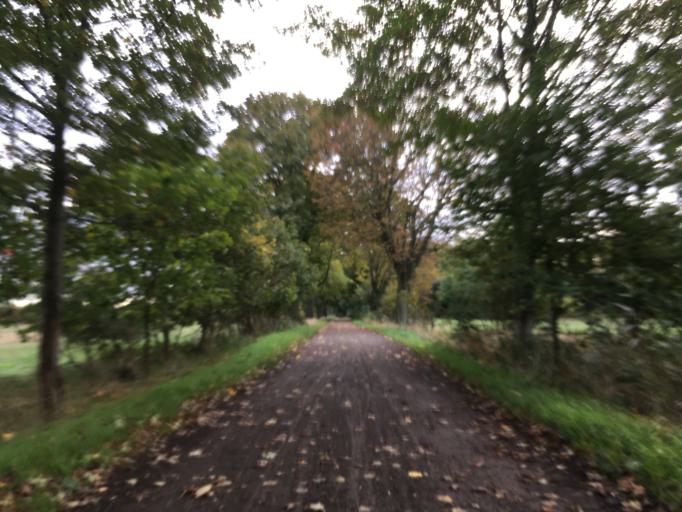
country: DE
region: Berlin
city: Karow
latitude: 52.5953
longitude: 13.4958
